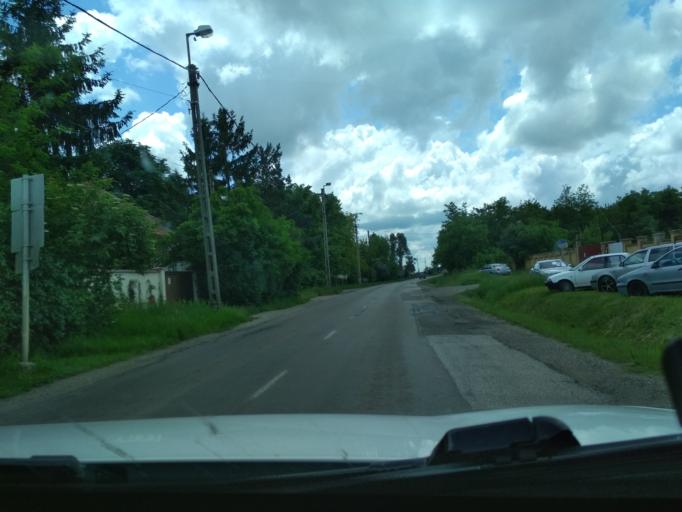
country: HU
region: Jasz-Nagykun-Szolnok
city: Tiszafured
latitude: 47.6060
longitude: 20.7630
